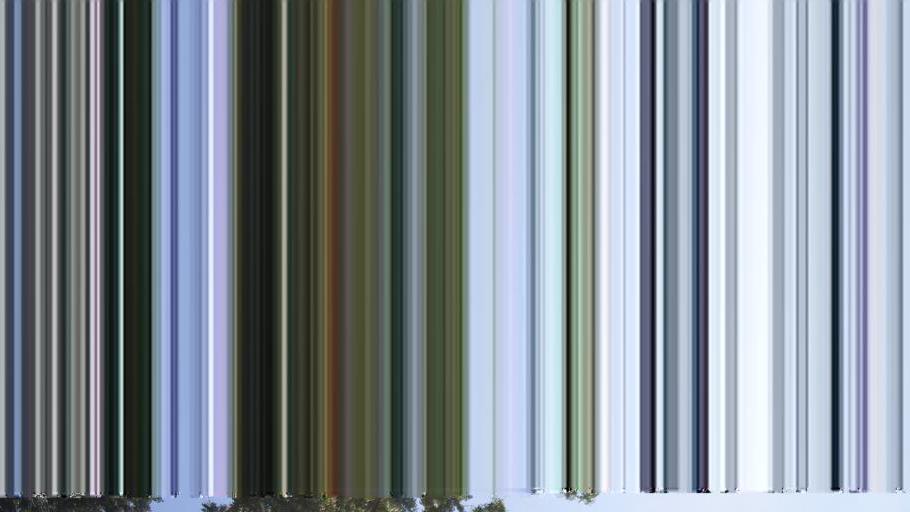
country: MY
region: Johor
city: Johor Bahru
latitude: 1.4157
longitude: 103.7549
